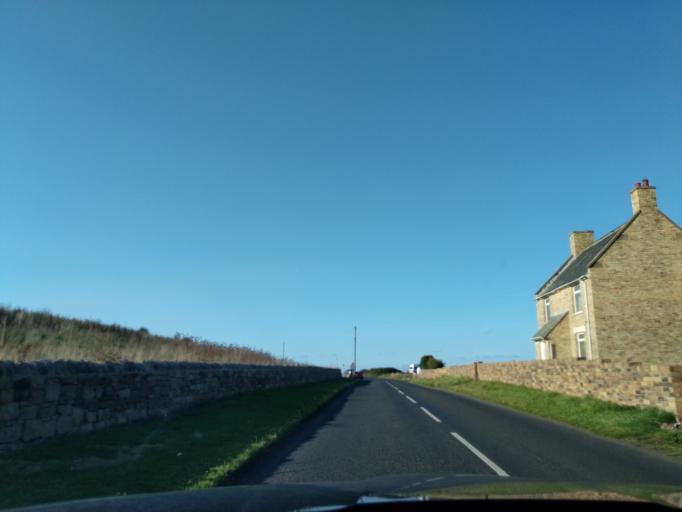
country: GB
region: England
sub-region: Northumberland
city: Lynemouth
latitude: 55.2274
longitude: -1.5291
